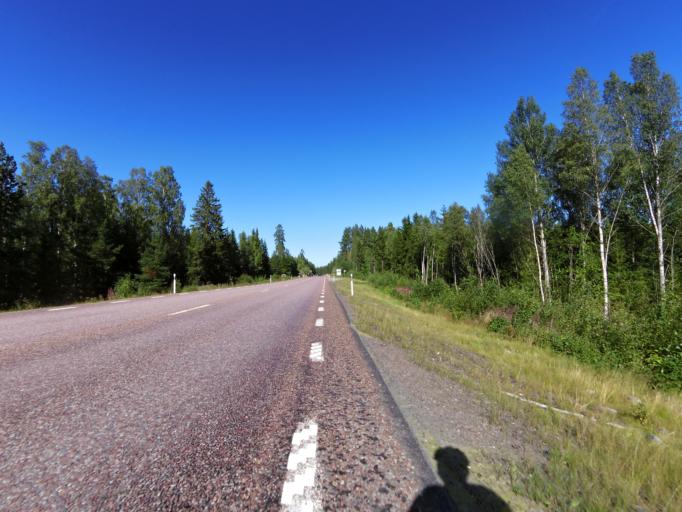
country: SE
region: Gaevleborg
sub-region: Hofors Kommun
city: Hofors
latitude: 60.5562
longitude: 16.4799
